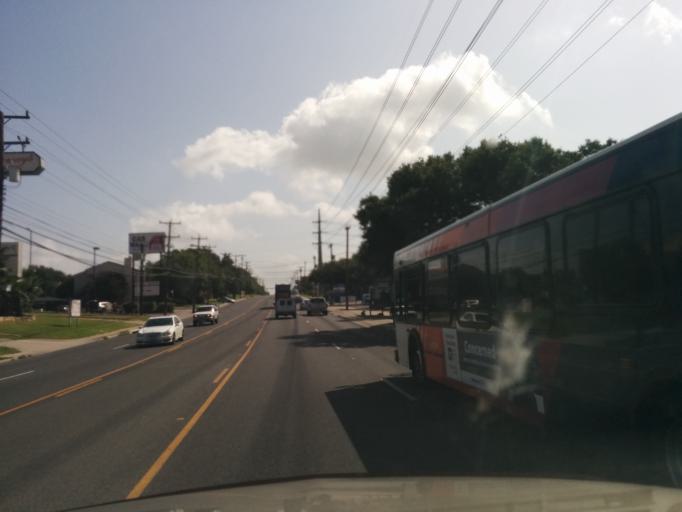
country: US
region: Texas
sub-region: Bexar County
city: Balcones Heights
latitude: 29.5252
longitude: -98.5682
